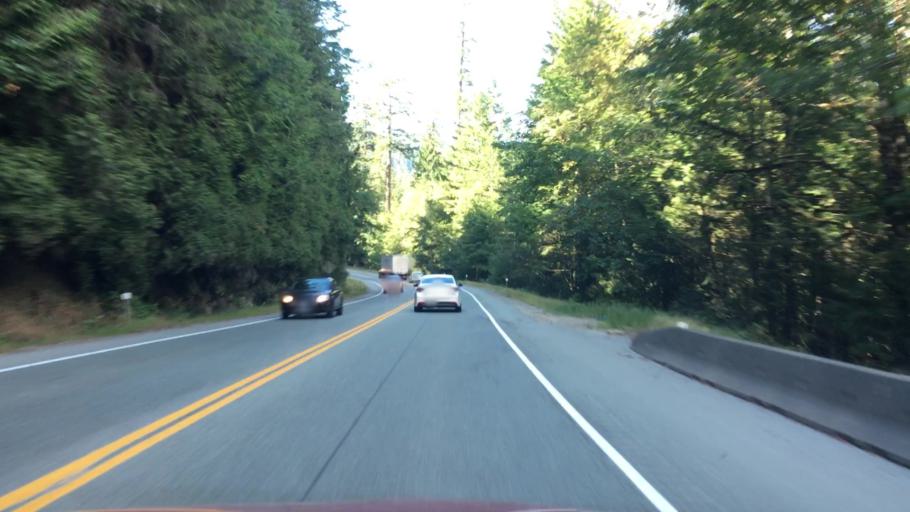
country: CA
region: British Columbia
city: Port Alberni
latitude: 49.2552
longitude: -124.6655
